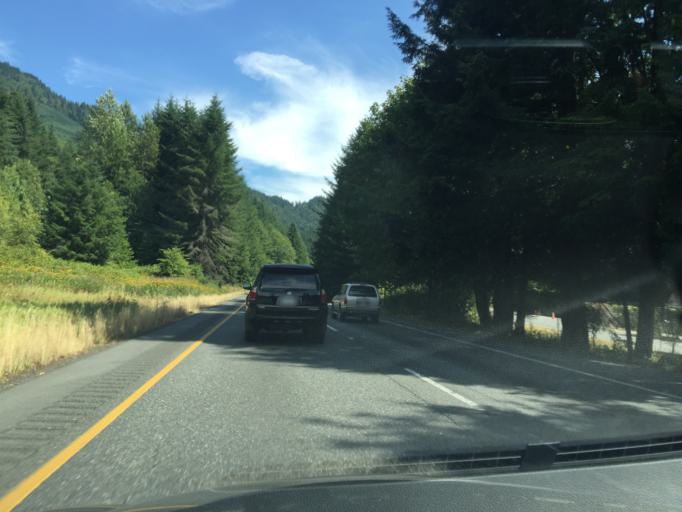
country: US
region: Washington
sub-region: Whatcom County
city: Sudden Valley
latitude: 48.6687
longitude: -122.3773
